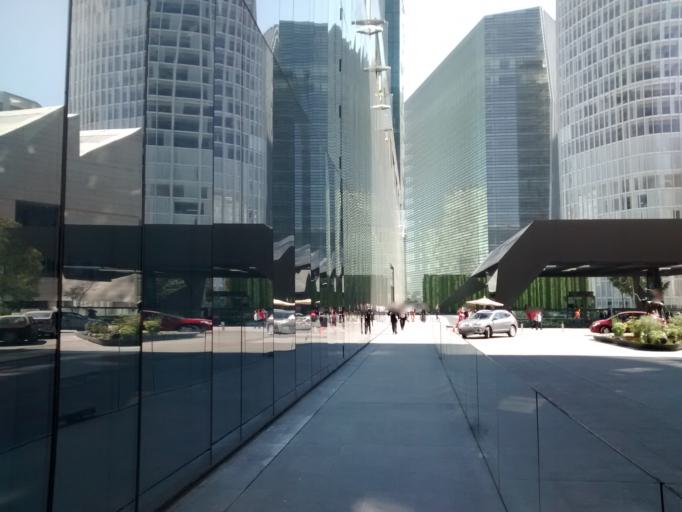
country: MX
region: Mexico City
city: Miguel Hidalgo
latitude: 19.4413
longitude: -99.2046
